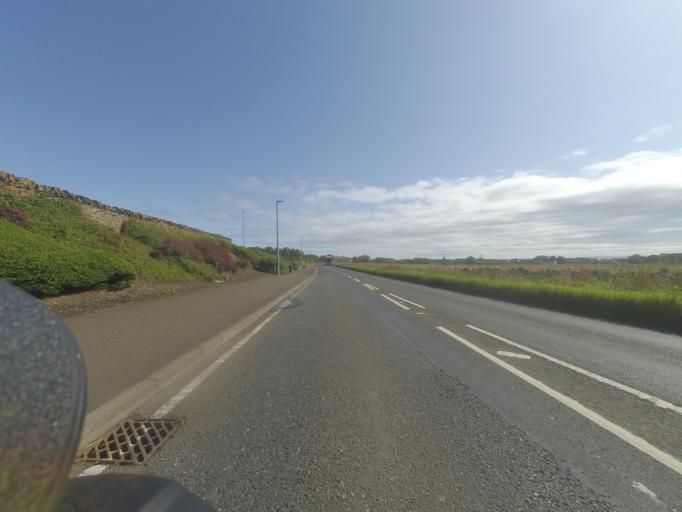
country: GB
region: Scotland
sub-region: Highland
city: Wick
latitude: 58.4513
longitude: -3.0996
